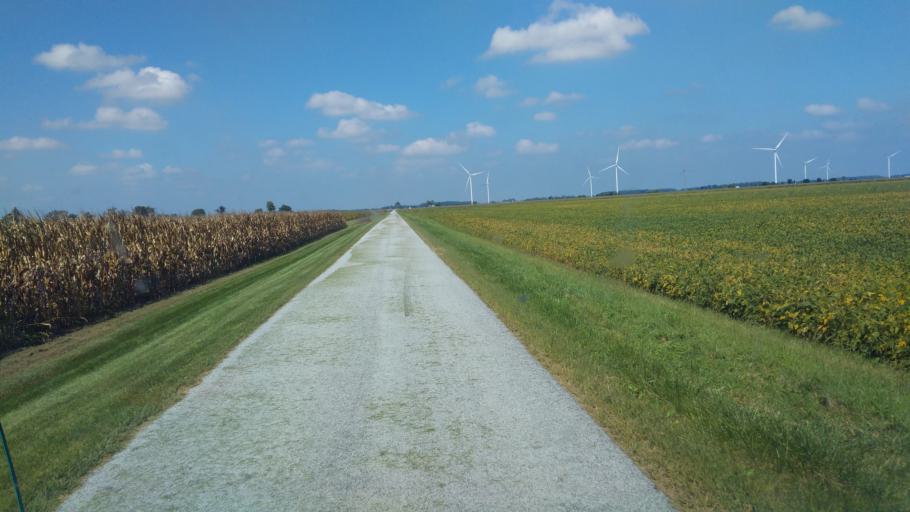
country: US
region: Ohio
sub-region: Hardin County
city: Ada
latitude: 40.7679
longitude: -83.7479
